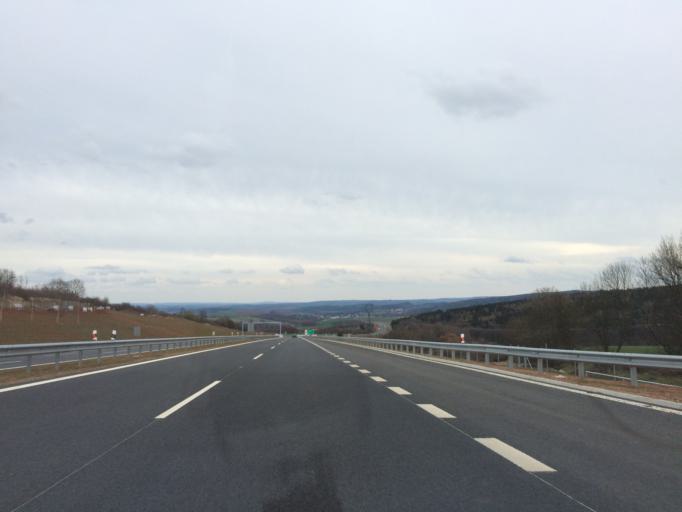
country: CZ
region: Ustecky
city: Lubenec
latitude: 50.1347
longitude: 13.2450
